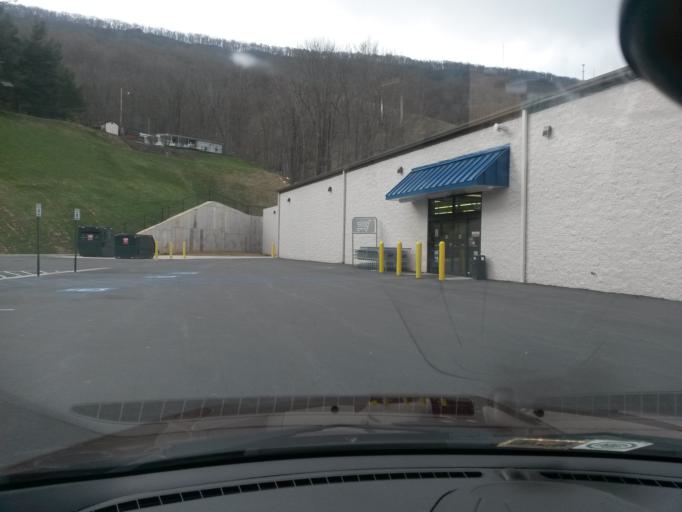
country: US
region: West Virginia
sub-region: Mercer County
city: Bluefield
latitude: 37.2690
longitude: -81.1722
